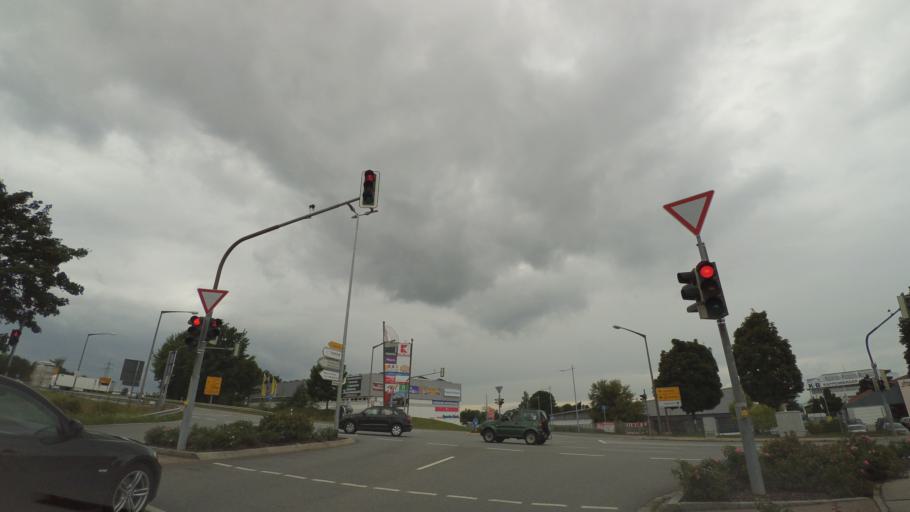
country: DE
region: Bavaria
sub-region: Upper Palatinate
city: Cham
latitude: 49.2017
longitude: 12.6624
